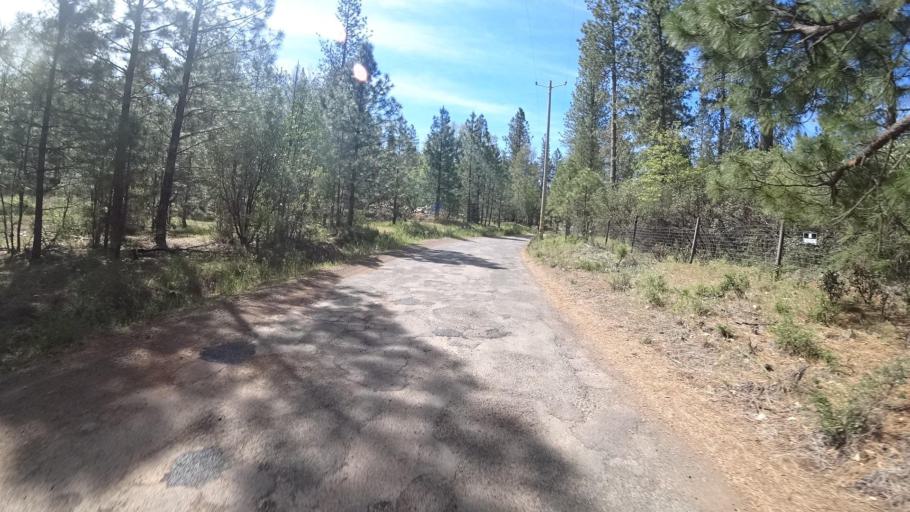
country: US
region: California
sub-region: Lake County
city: Cobb
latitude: 38.8783
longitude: -122.7670
